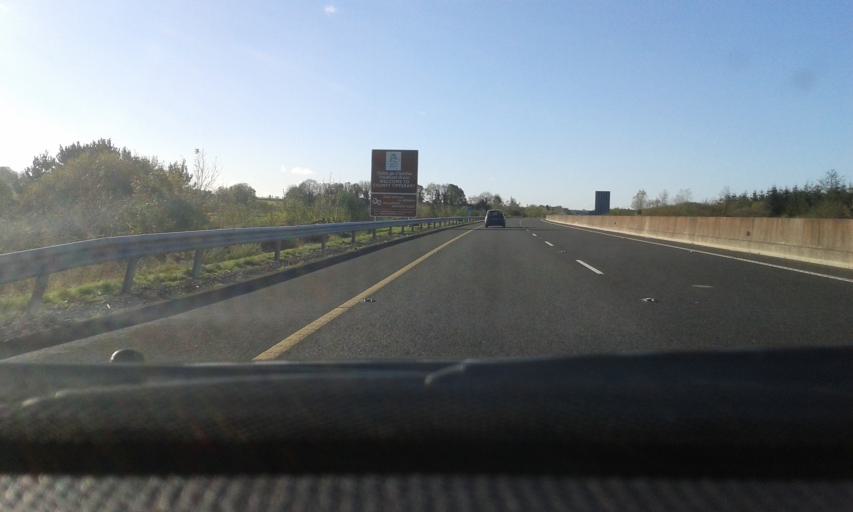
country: IE
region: Leinster
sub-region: Laois
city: Rathdowney
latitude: 52.7209
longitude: -7.5974
